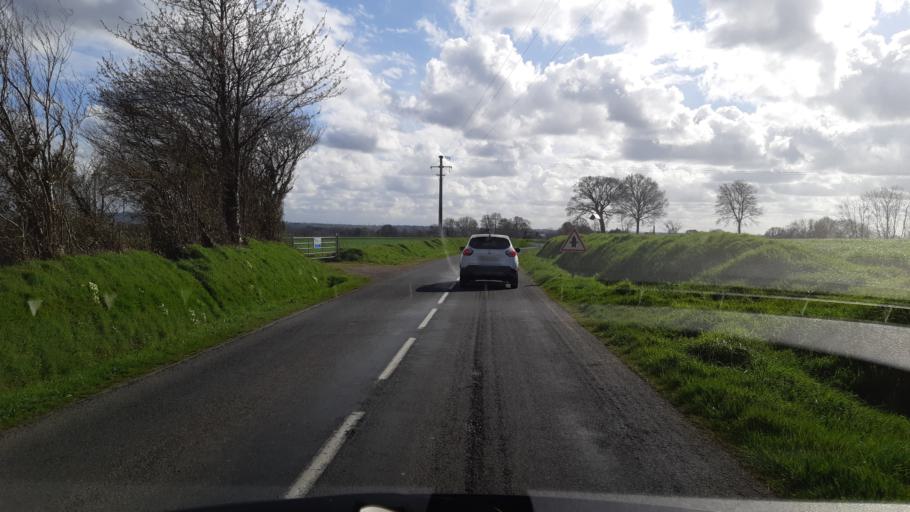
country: FR
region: Lower Normandy
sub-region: Departement de la Manche
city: Percy
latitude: 49.0199
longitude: -1.1610
